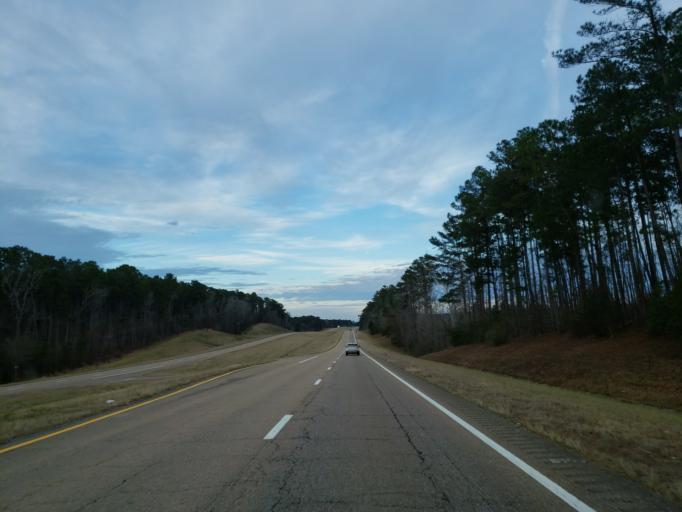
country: US
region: Mississippi
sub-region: Lauderdale County
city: Meridian Station
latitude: 32.4817
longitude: -88.5962
